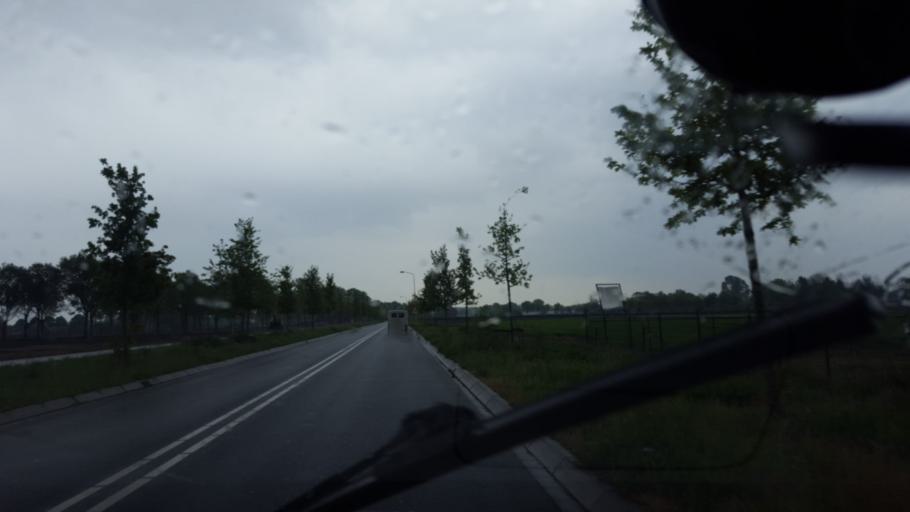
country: NL
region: North Brabant
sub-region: Gemeente Someren
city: Someren
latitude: 51.3759
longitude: 5.7104
